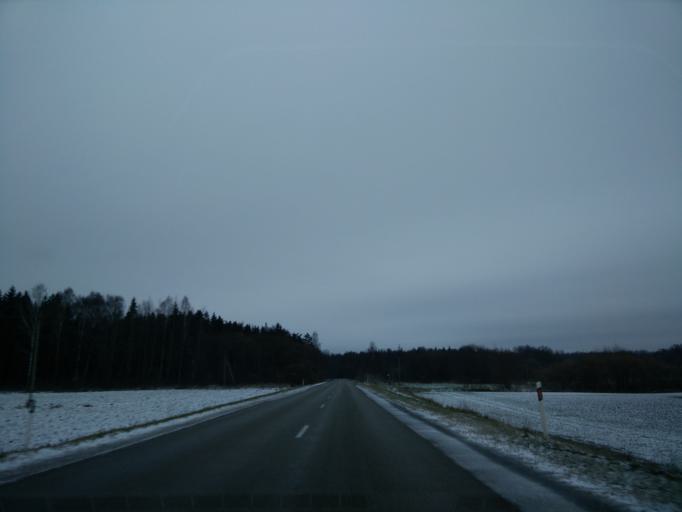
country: LT
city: Ariogala
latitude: 55.4103
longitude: 23.3411
